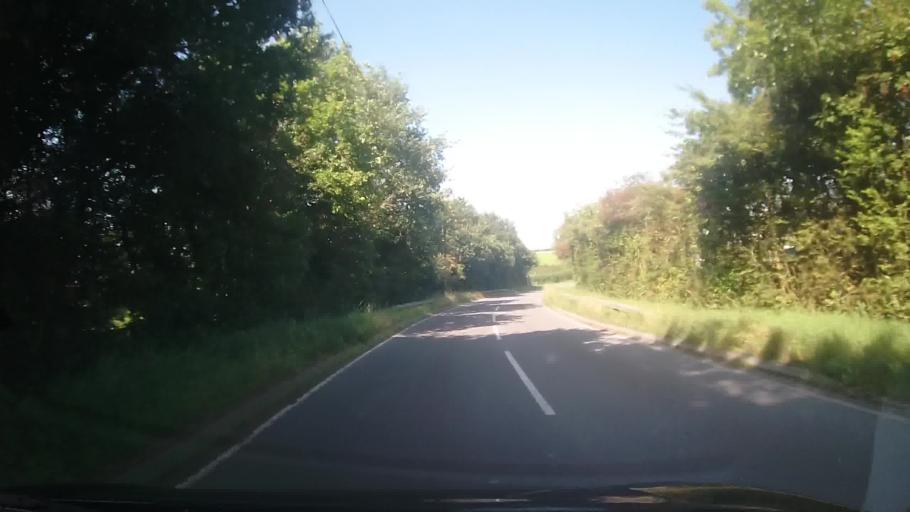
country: GB
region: Wales
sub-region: Pembrokeshire
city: Camrose
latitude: 51.8532
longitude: -5.0127
